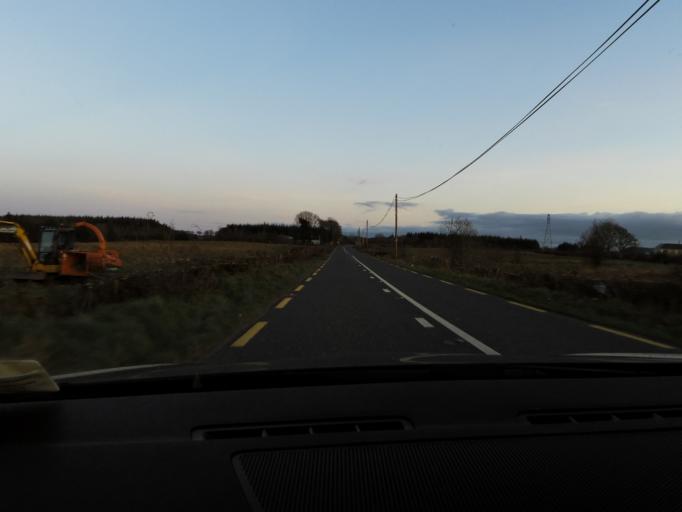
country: IE
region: Connaught
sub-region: Roscommon
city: Boyle
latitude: 53.9201
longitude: -8.2743
